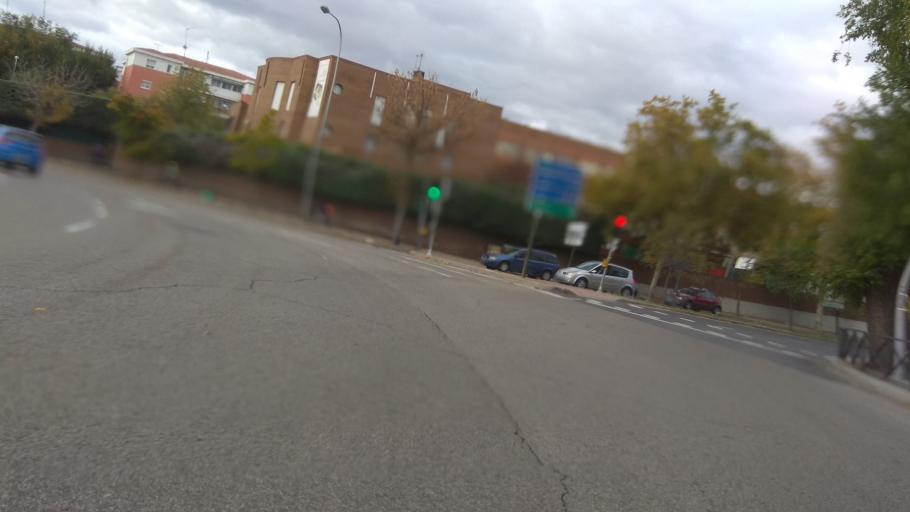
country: ES
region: Madrid
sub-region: Provincia de Madrid
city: Vicalvaro
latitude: 40.4099
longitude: -3.6095
